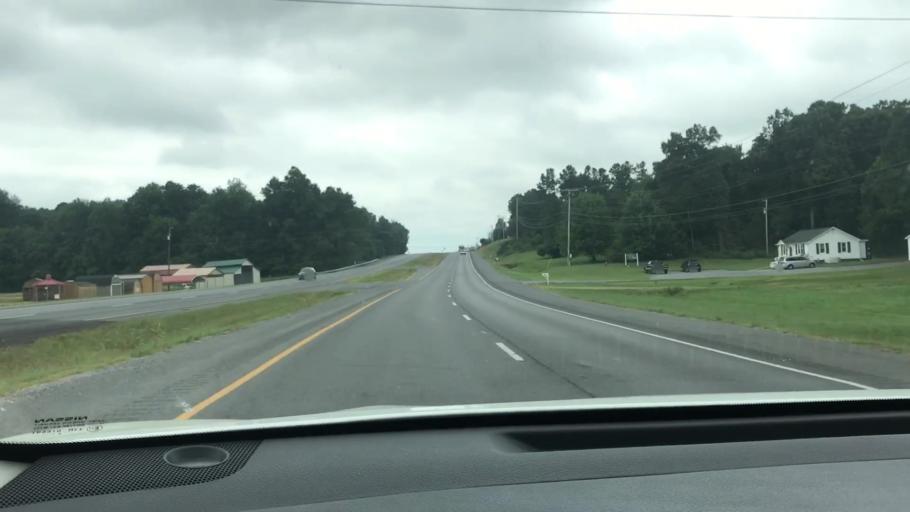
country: US
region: Kentucky
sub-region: Calloway County
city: Murray
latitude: 36.6735
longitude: -88.3028
